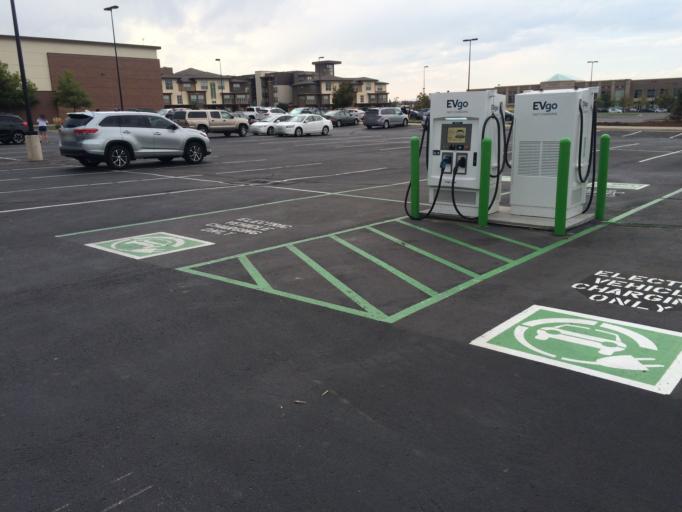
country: US
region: Colorado
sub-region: Adams County
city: Northglenn
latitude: 39.9632
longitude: -104.9899
